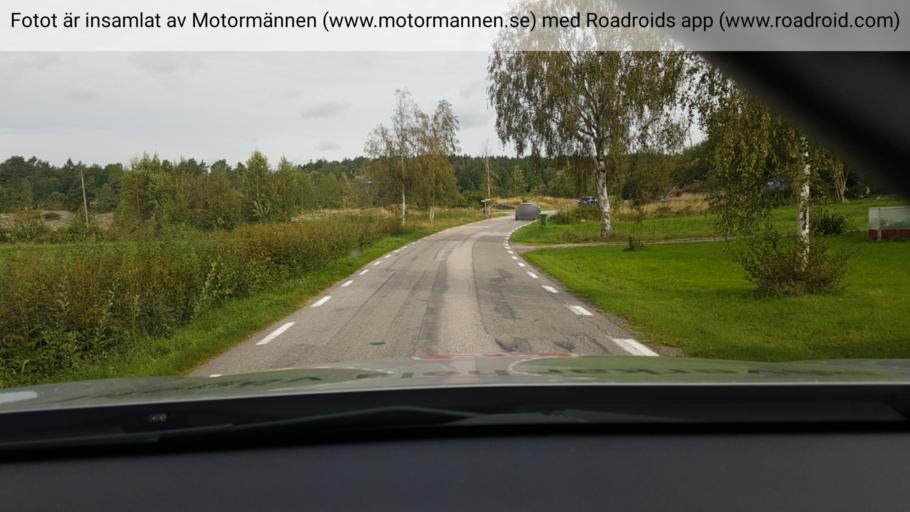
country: SE
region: Vaestra Goetaland
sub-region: Orust
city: Henan
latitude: 58.2444
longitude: 11.5545
